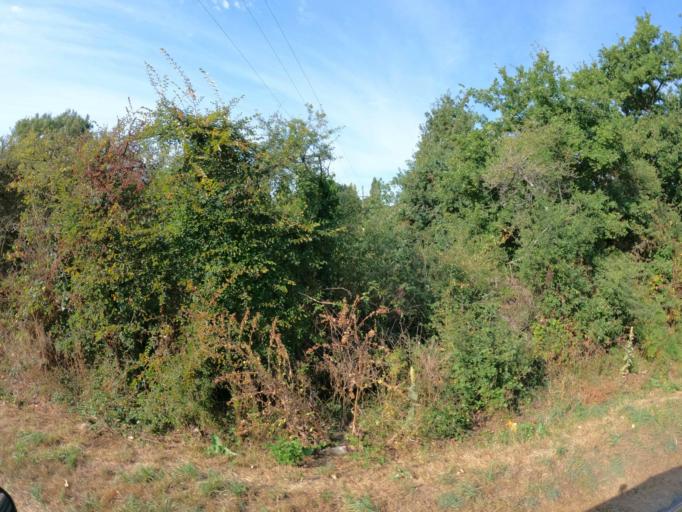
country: FR
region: Pays de la Loire
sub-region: Departement de la Vendee
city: Saint-Christophe-du-Ligneron
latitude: 46.8049
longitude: -1.7997
